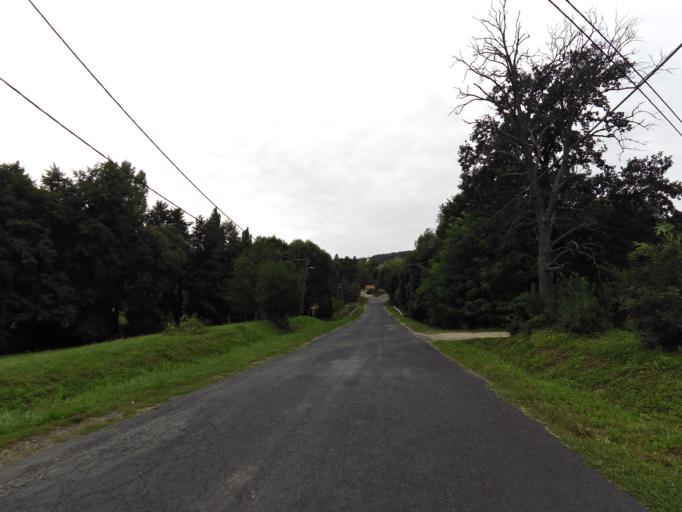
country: HU
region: Zala
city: Gyenesdias
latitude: 46.8466
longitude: 17.3037
